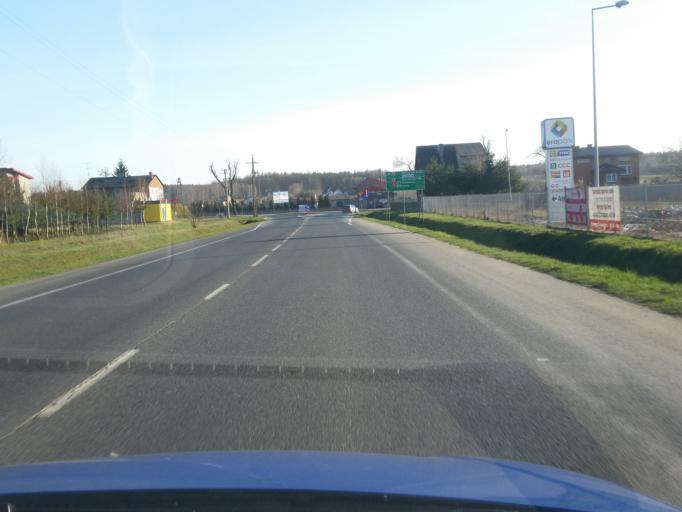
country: PL
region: Lodz Voivodeship
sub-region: Powiat radomszczanski
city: Radomsko
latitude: 51.0804
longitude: 19.3790
